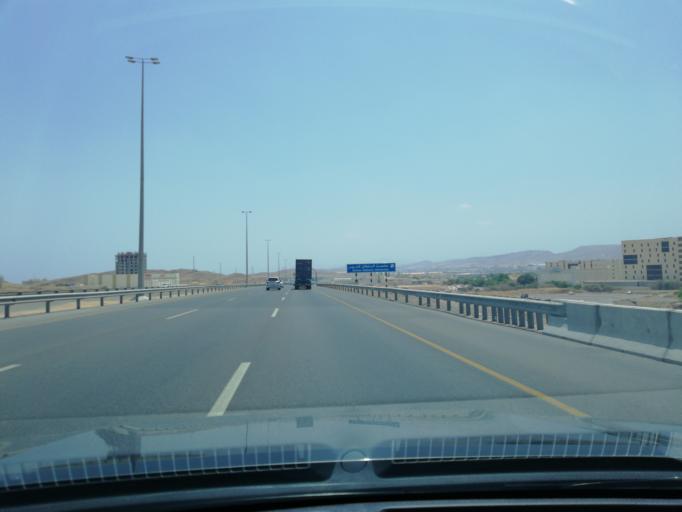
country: OM
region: Muhafazat Masqat
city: As Sib al Jadidah
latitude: 23.5692
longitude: 58.1718
